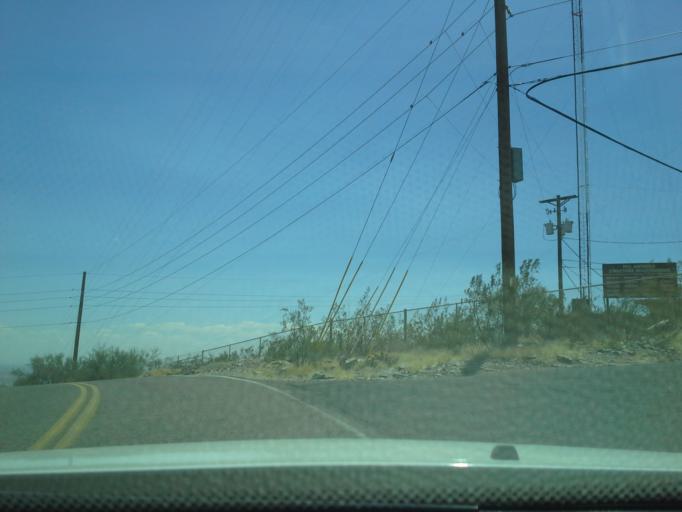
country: US
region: Arizona
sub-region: Maricopa County
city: Guadalupe
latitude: 33.3318
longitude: -112.0632
